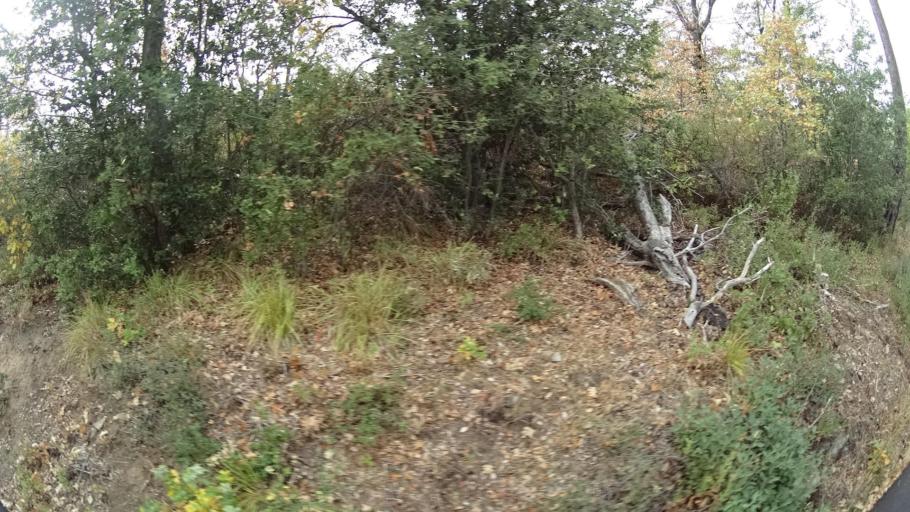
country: US
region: California
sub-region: San Diego County
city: Julian
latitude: 33.0541
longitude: -116.6256
